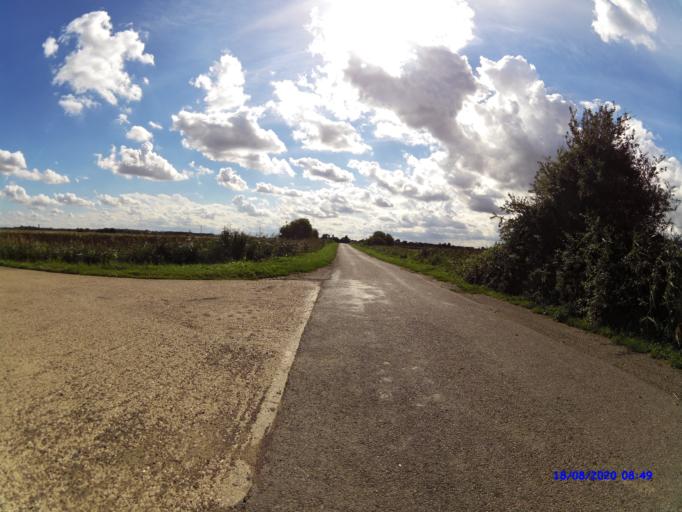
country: GB
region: England
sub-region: Cambridgeshire
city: Ramsey
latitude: 52.4858
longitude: -0.0967
